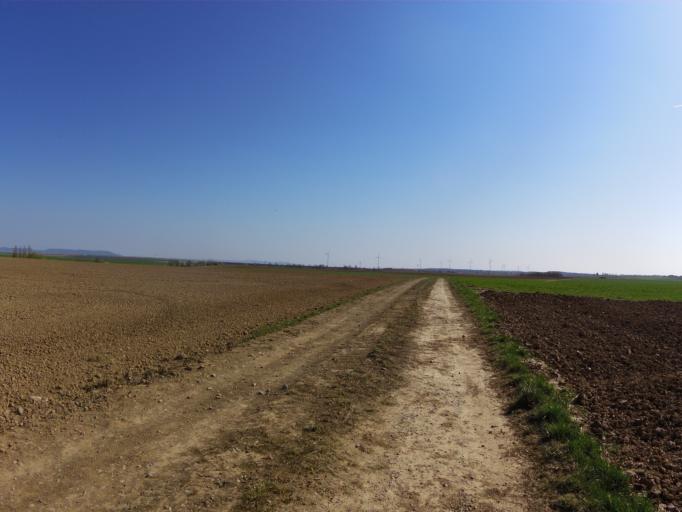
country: DE
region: Bavaria
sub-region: Regierungsbezirk Unterfranken
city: Biebelried
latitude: 49.8187
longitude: 10.1014
